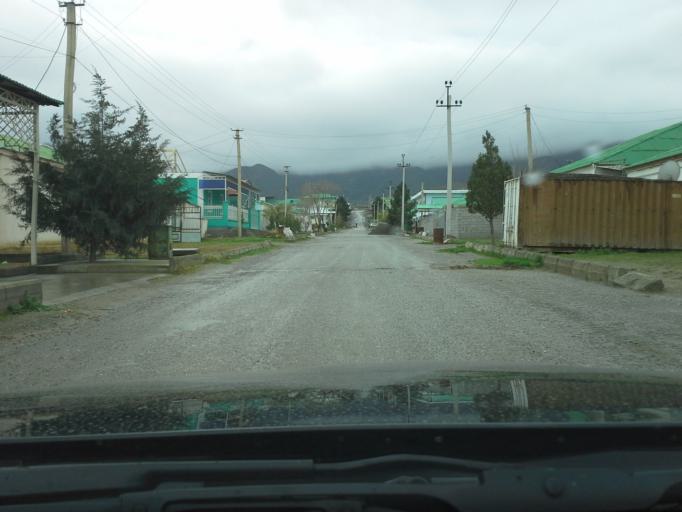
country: TM
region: Ahal
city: Abadan
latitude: 37.9640
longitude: 58.2055
